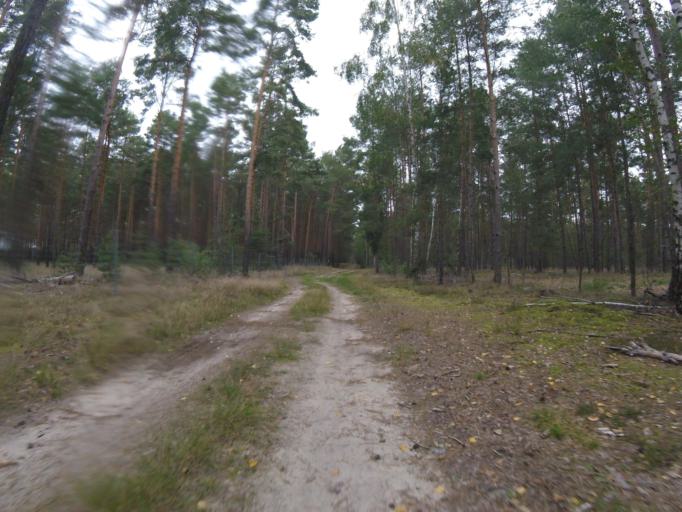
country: DE
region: Brandenburg
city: Gross Koris
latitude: 52.1834
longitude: 13.6769
